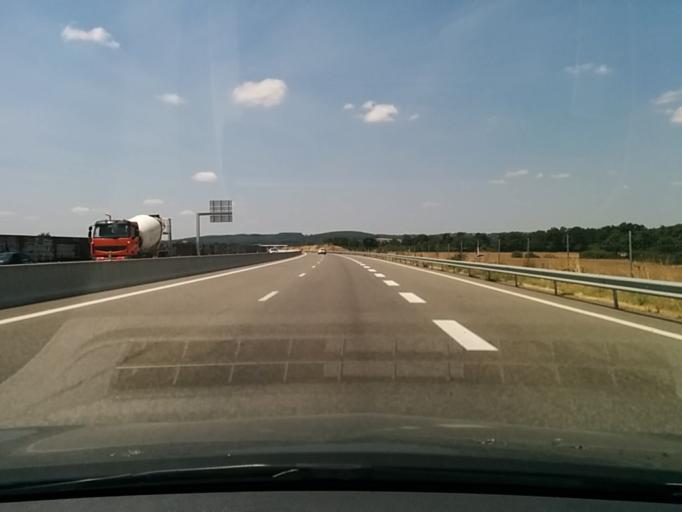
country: FR
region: Midi-Pyrenees
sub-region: Departement de la Haute-Garonne
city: Leguevin
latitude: 43.5825
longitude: 1.2139
